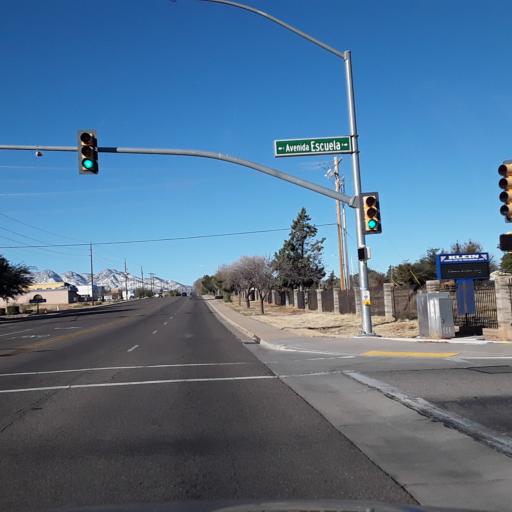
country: US
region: Arizona
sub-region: Cochise County
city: Sierra Vista
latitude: 31.5547
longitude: -110.2618
